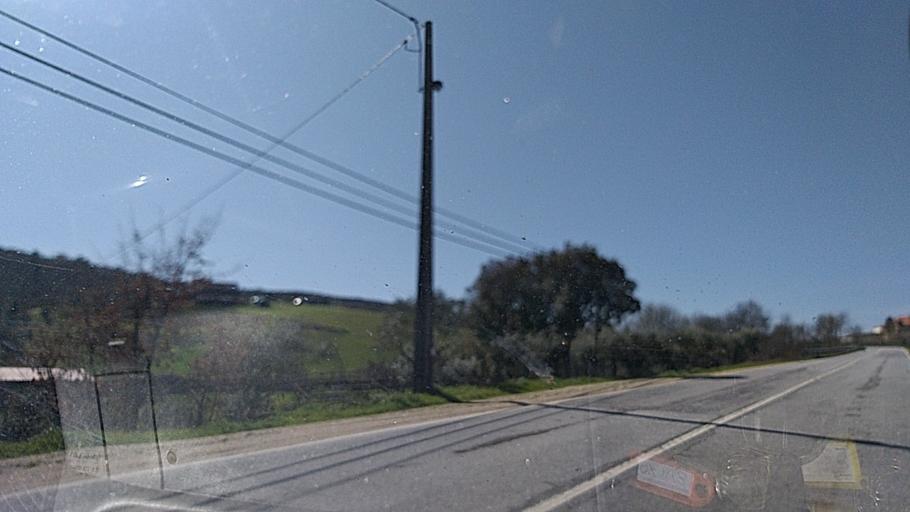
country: PT
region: Guarda
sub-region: Celorico da Beira
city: Celorico da Beira
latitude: 40.5980
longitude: -7.4282
